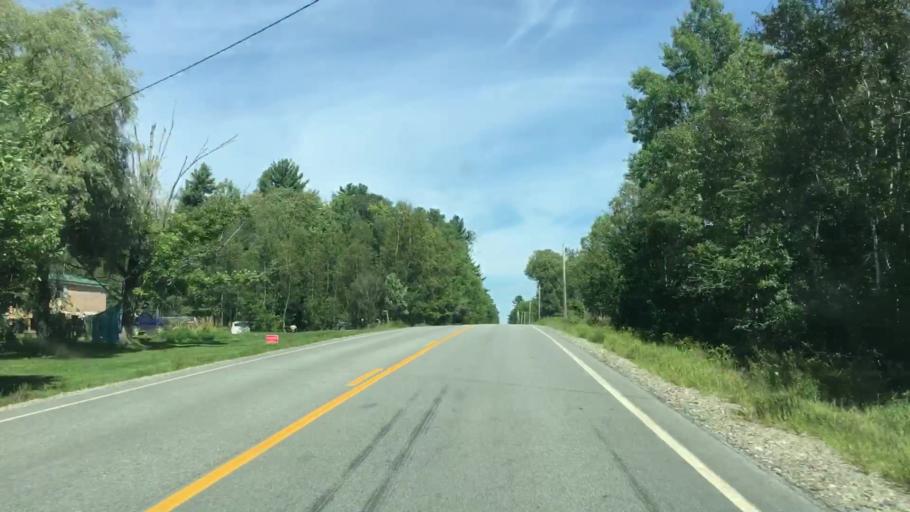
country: US
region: Maine
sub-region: Penobscot County
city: Howland
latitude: 45.2134
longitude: -68.7967
